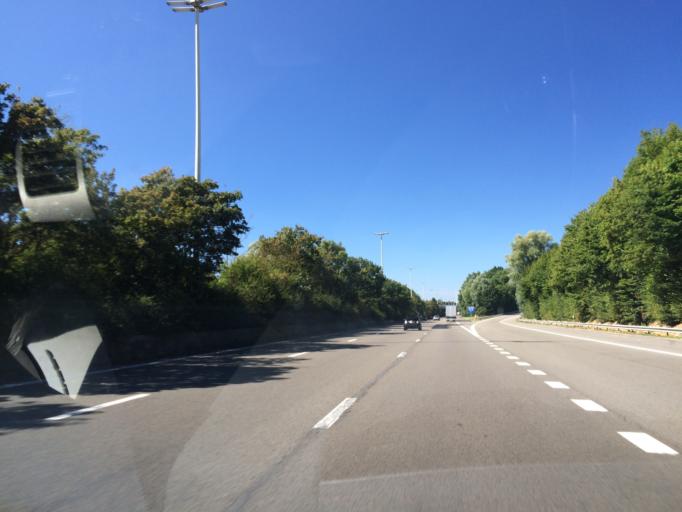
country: BE
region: Wallonia
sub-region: Province du Brabant Wallon
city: Perwez
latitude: 50.5592
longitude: 4.8380
